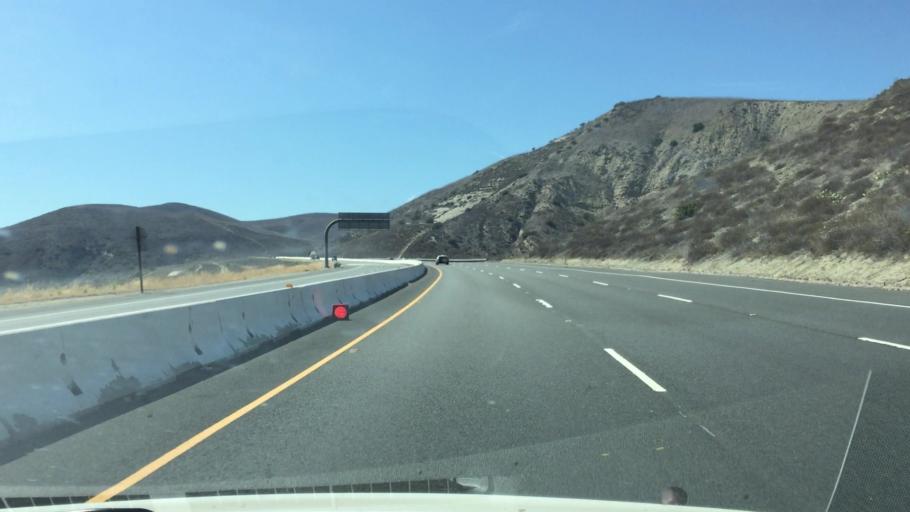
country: US
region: California
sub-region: Orange County
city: North Tustin
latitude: 33.7464
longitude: -117.7213
